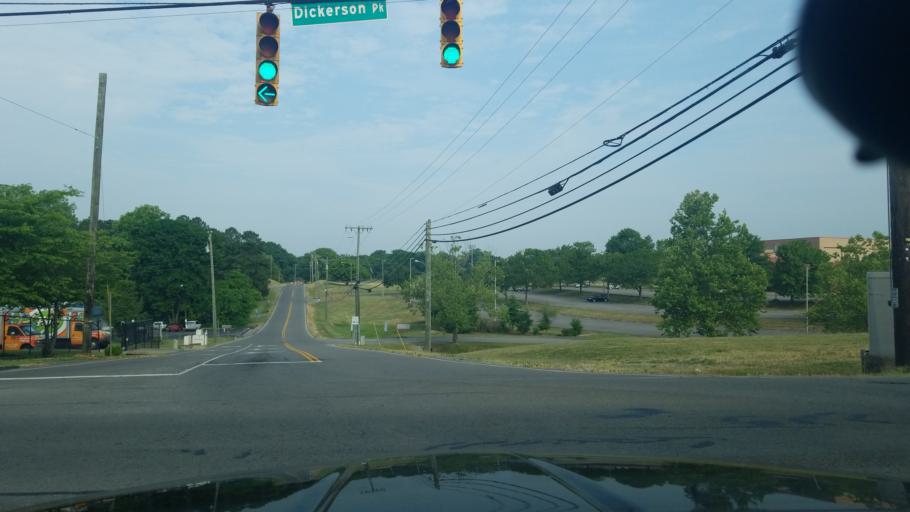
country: US
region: Tennessee
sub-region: Davidson County
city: Goodlettsville
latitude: 36.2777
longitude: -86.7512
